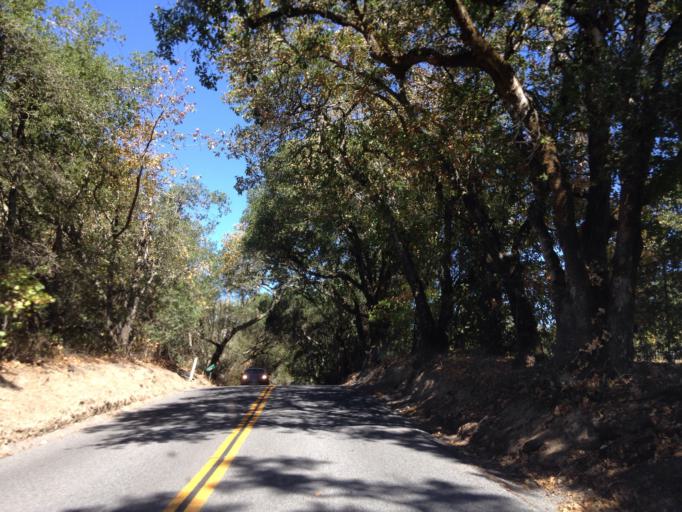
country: US
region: California
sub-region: Sonoma County
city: Forestville
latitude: 38.5004
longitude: -122.8574
